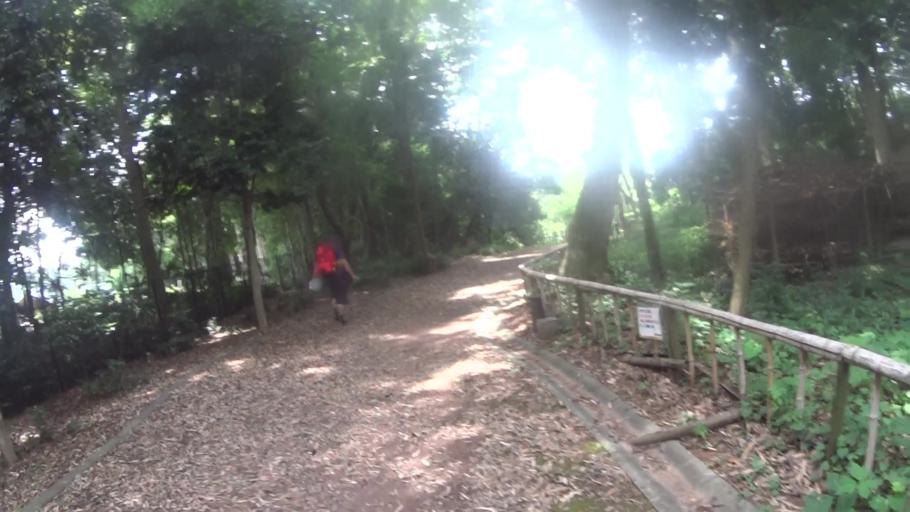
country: JP
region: Saitama
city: Ageoshimo
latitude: 35.9369
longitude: 139.5655
